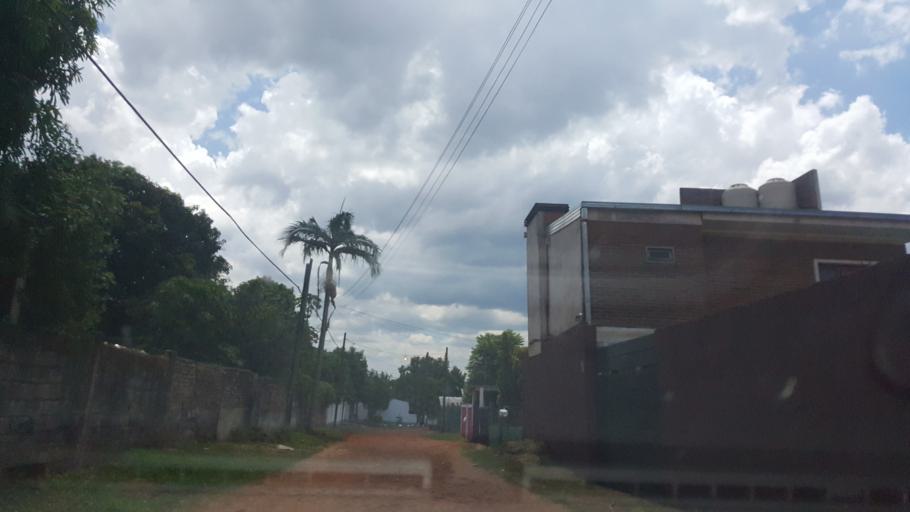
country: AR
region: Misiones
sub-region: Departamento de Capital
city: Posadas
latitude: -27.4094
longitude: -55.9106
